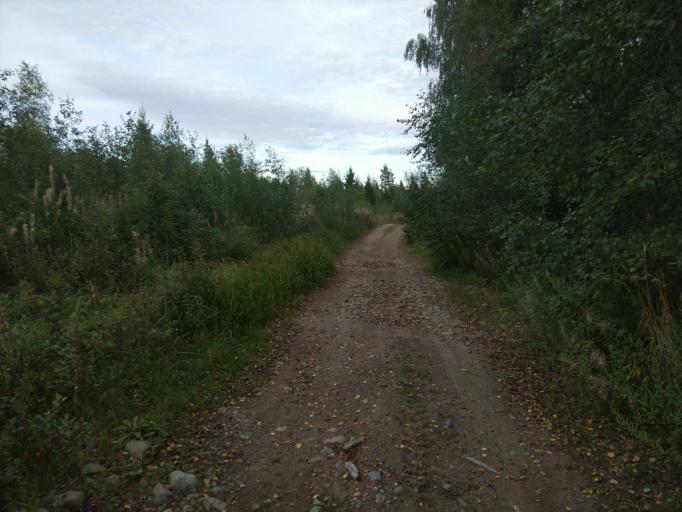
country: RU
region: Leningrad
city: Kuznechnoye
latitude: 61.1178
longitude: 29.6005
